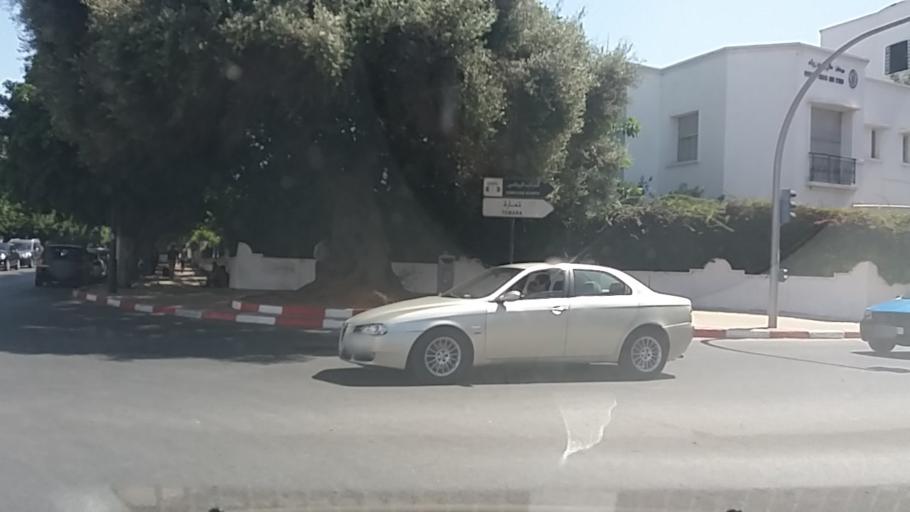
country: MA
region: Rabat-Sale-Zemmour-Zaer
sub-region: Rabat
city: Rabat
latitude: 34.0173
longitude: -6.8283
